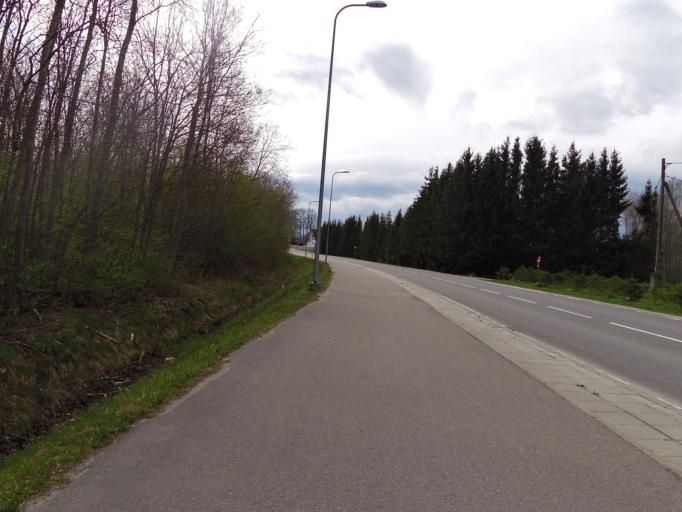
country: EE
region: Harju
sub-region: Rae vald
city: Jueri
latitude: 59.3773
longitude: 24.8422
